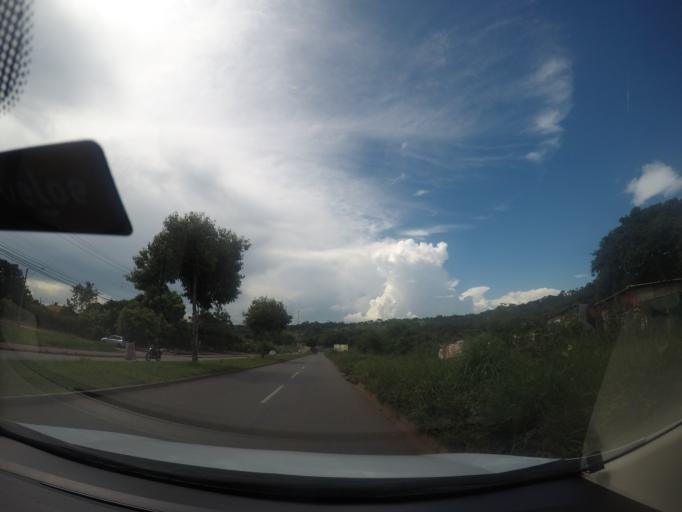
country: BR
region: Goias
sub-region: Trindade
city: Trindade
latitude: -16.6735
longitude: -49.3858
